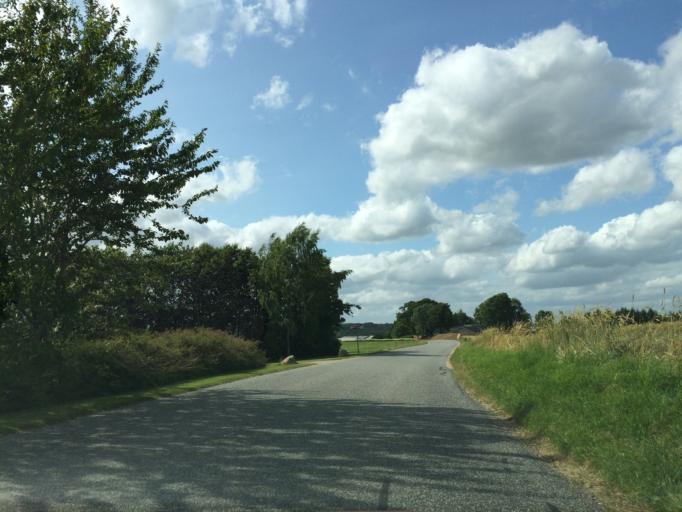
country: DK
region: Central Jutland
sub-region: Favrskov Kommune
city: Hammel
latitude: 56.2167
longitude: 9.7497
